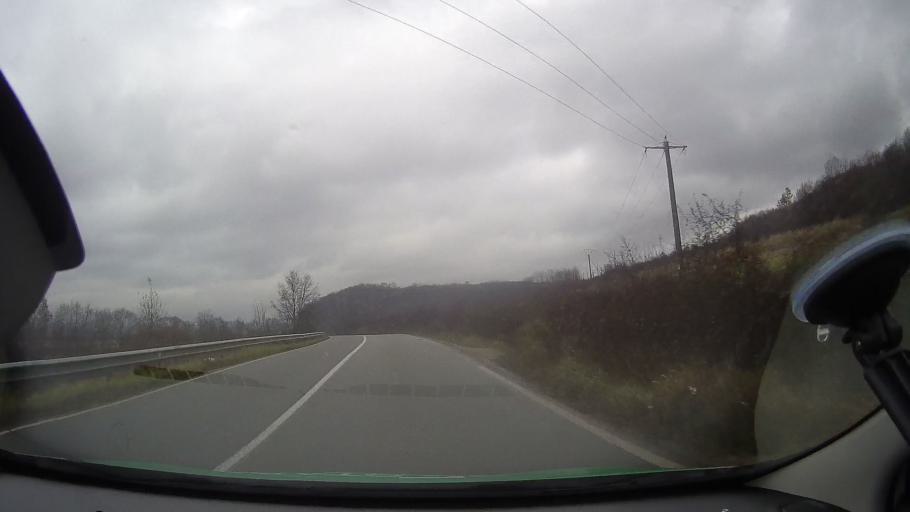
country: RO
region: Arad
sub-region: Comuna Almas
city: Almas
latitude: 46.3005
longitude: 22.1899
